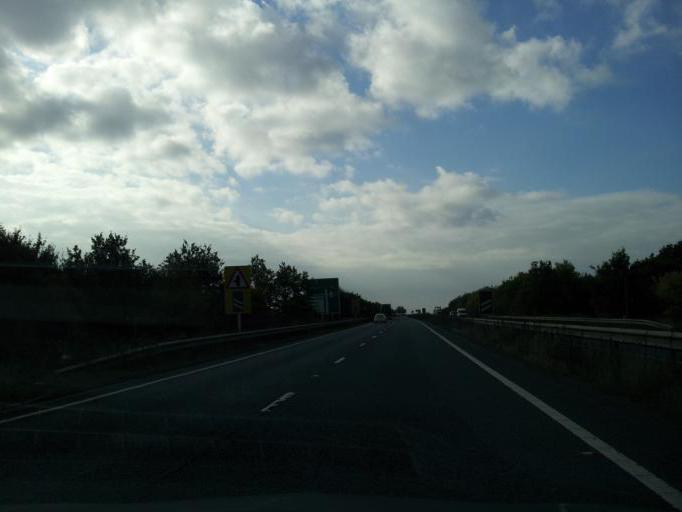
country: GB
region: England
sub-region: Northamptonshire
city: Blisworth
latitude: 52.1682
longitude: -0.9599
